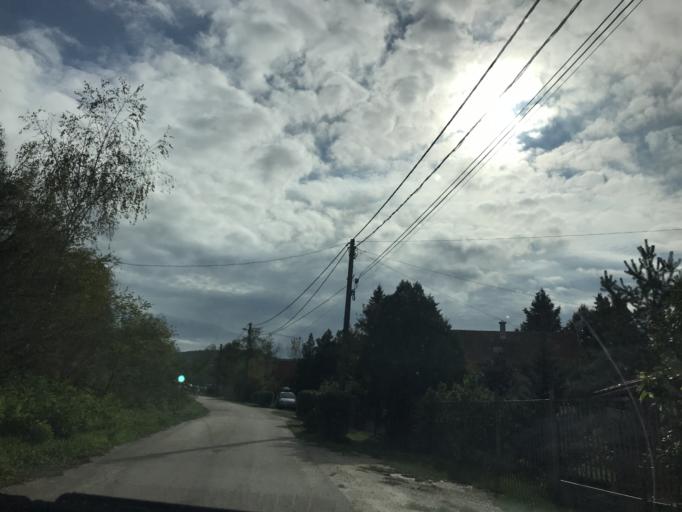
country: HU
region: Komarom-Esztergom
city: Piliscsev
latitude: 47.6728
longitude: 18.7937
